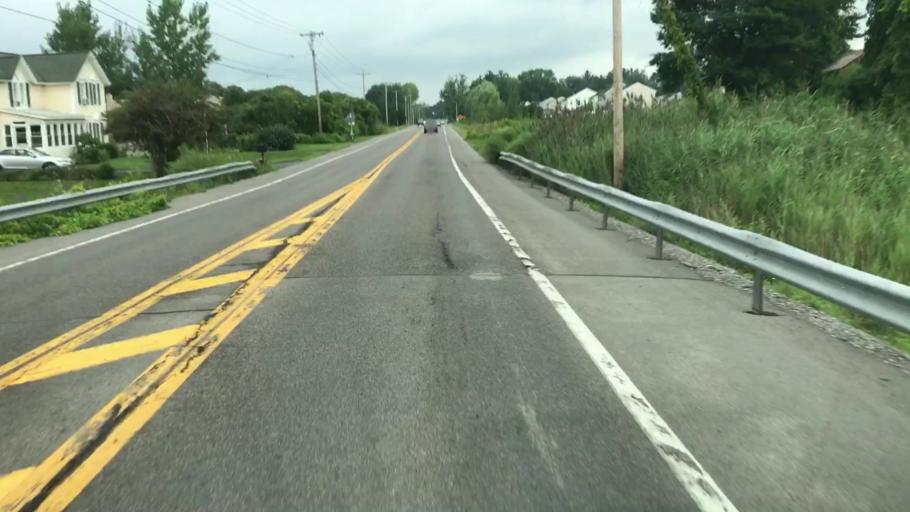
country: US
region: New York
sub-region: Onondaga County
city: Liverpool
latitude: 43.1647
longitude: -76.2087
